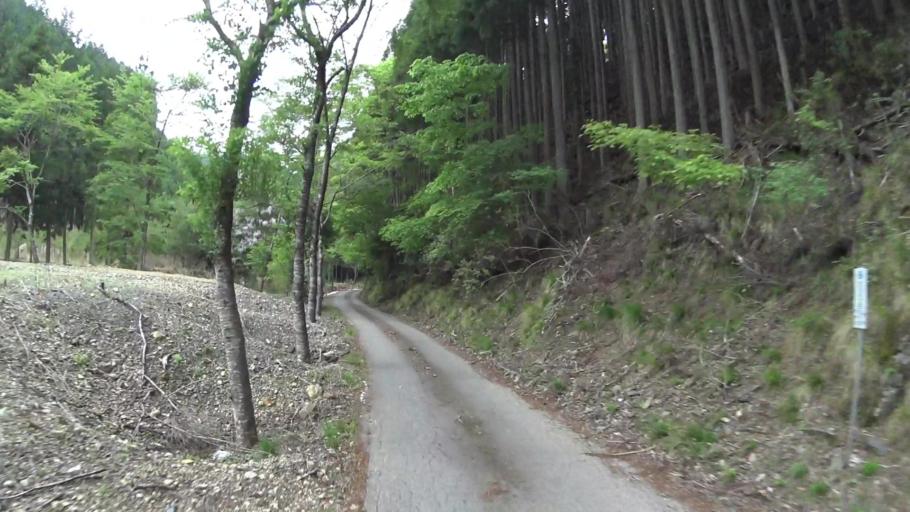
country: JP
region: Kyoto
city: Kameoka
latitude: 35.1171
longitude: 135.6272
